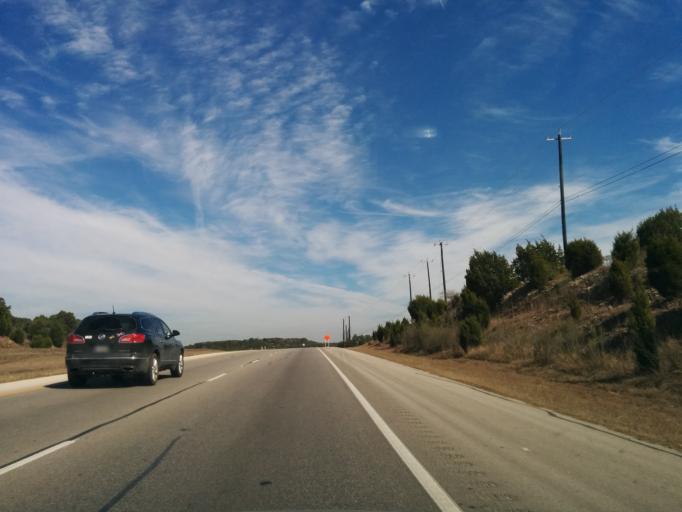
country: US
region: Texas
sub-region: Comal County
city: Bulverde
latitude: 29.7642
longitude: -98.4290
